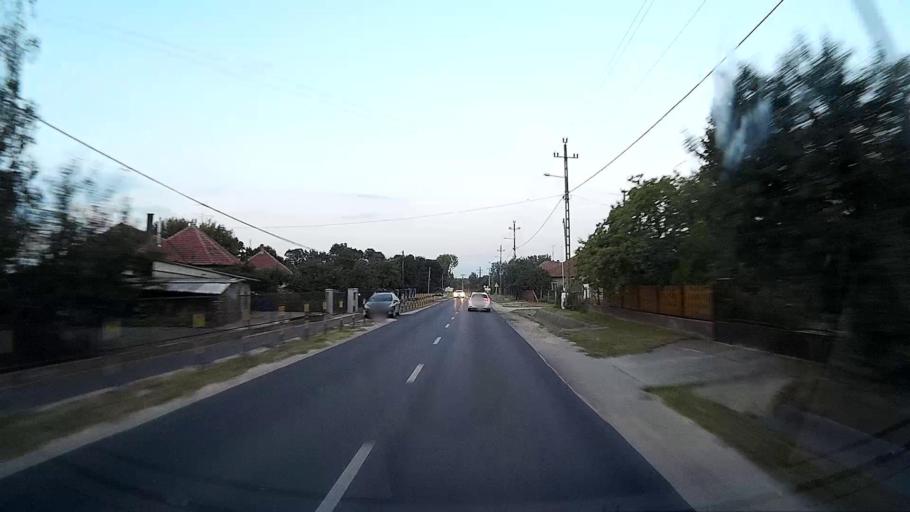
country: HU
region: Pest
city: Albertirsa
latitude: 47.2436
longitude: 19.6229
